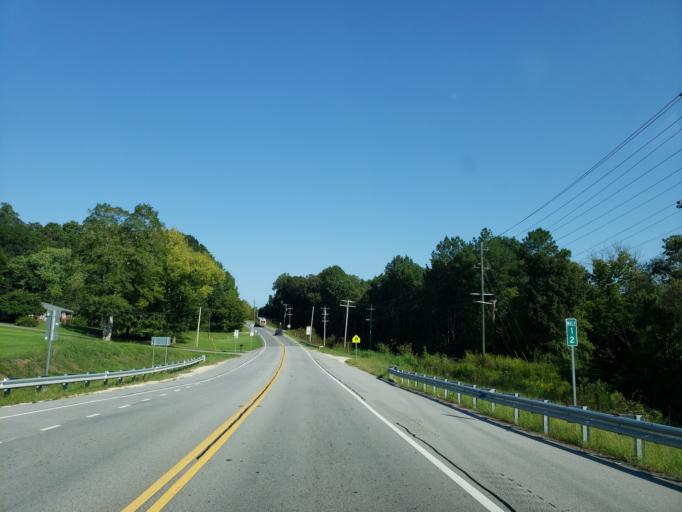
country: US
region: Georgia
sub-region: Catoosa County
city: Ringgold
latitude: 34.9058
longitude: -85.0767
